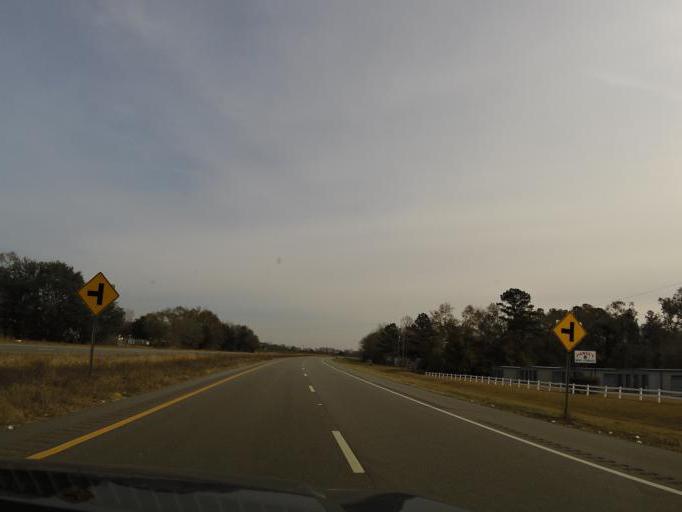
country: US
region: Alabama
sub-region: Houston County
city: Ashford
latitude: 31.1677
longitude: -85.2029
